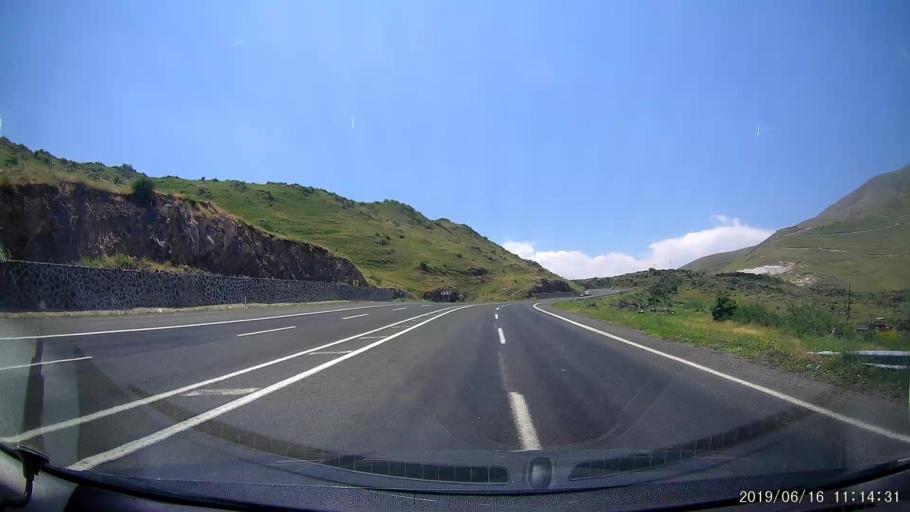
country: TR
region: Igdir
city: Igdir
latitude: 39.7774
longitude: 44.1423
